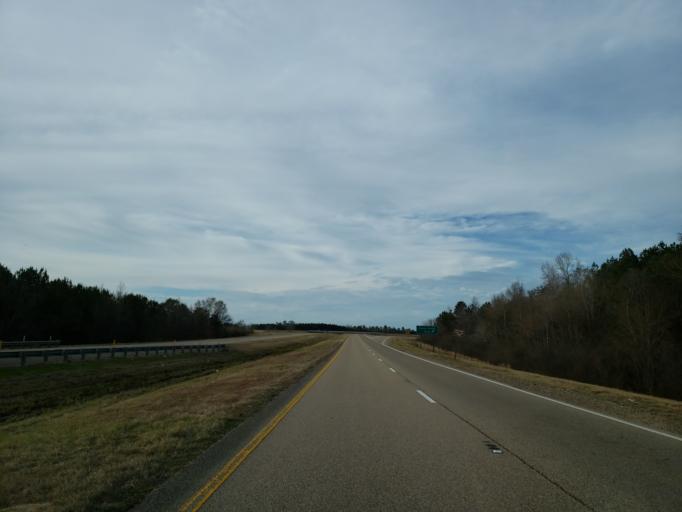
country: US
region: Mississippi
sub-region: Wayne County
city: Waynesboro
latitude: 31.6761
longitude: -88.6105
